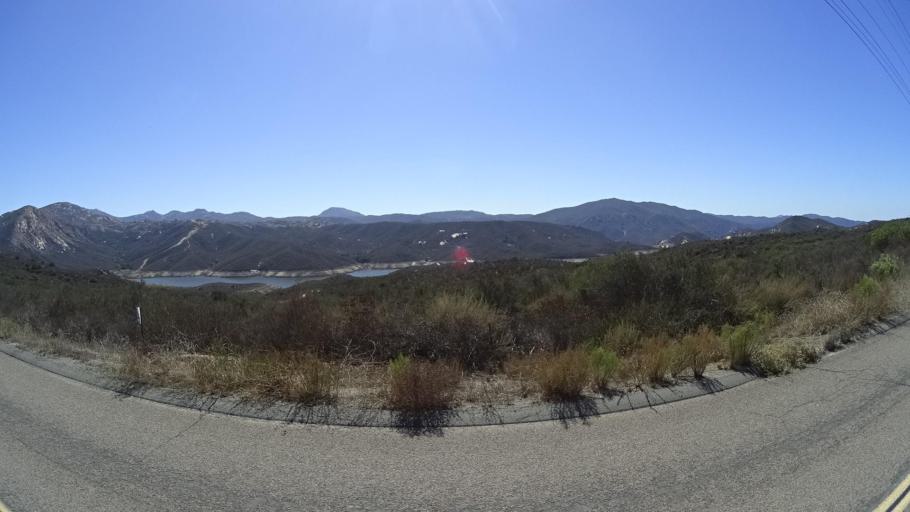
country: US
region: California
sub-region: San Diego County
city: Alpine
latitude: 32.7980
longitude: -116.7755
